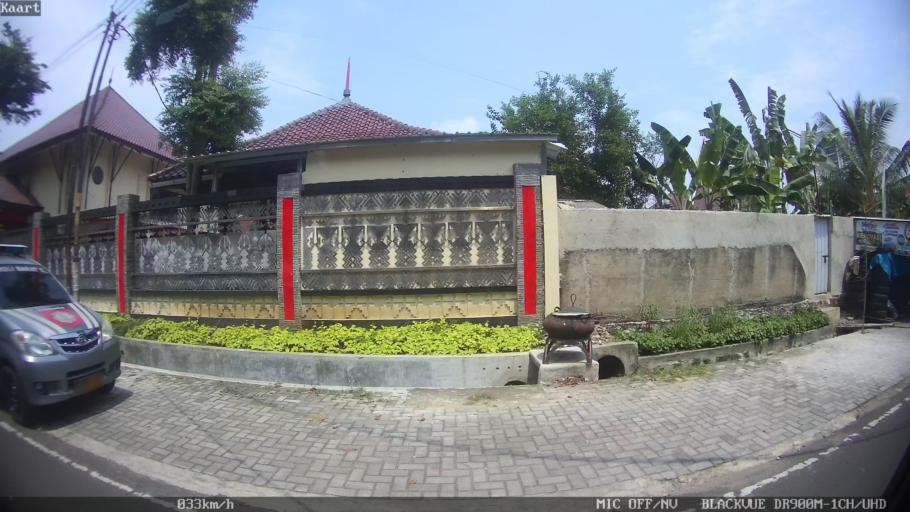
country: ID
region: Lampung
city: Bandarlampung
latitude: -5.4248
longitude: 105.2717
